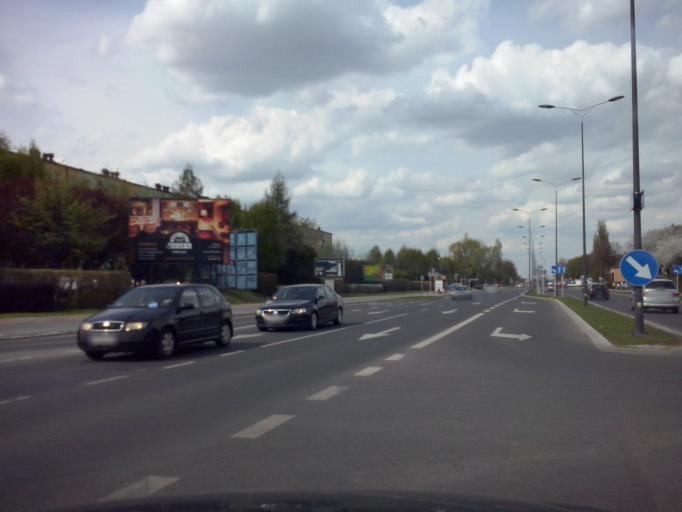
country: PL
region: Subcarpathian Voivodeship
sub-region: Rzeszow
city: Rzeszow
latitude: 50.0306
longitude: 22.0170
